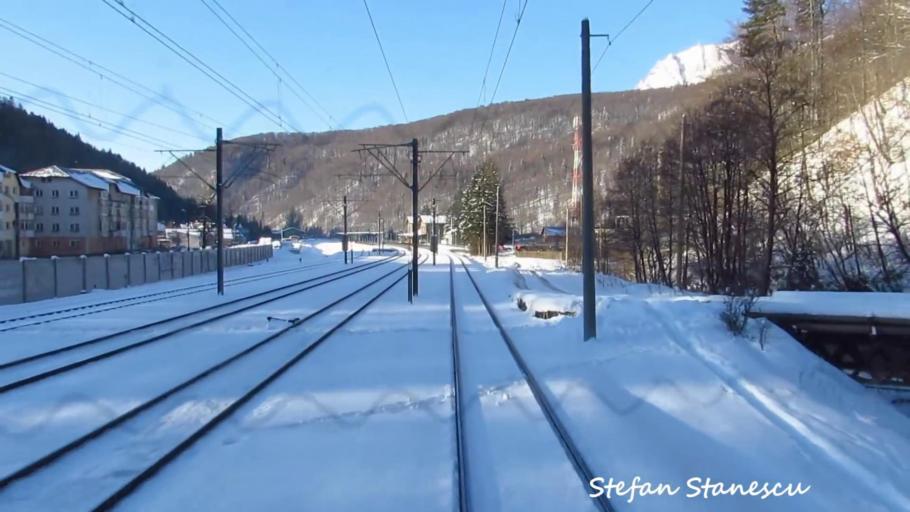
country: RO
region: Prahova
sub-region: Oras Azuga
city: Azuga
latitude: 45.4469
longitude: 25.5543
